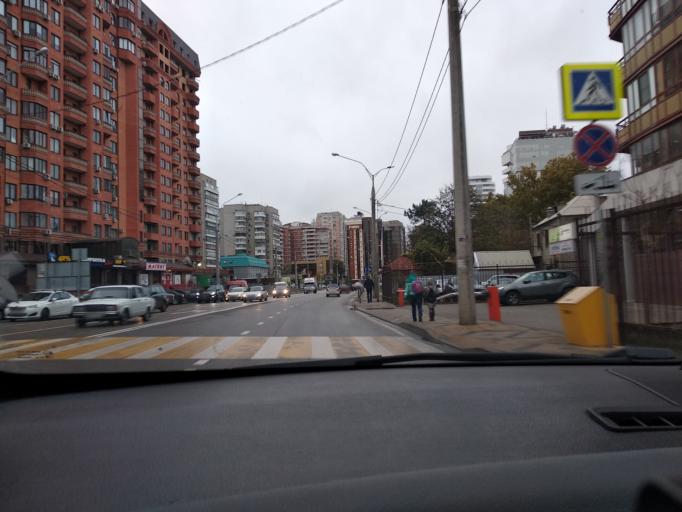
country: RU
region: Krasnodarskiy
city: Krasnodar
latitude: 45.0208
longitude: 38.9598
